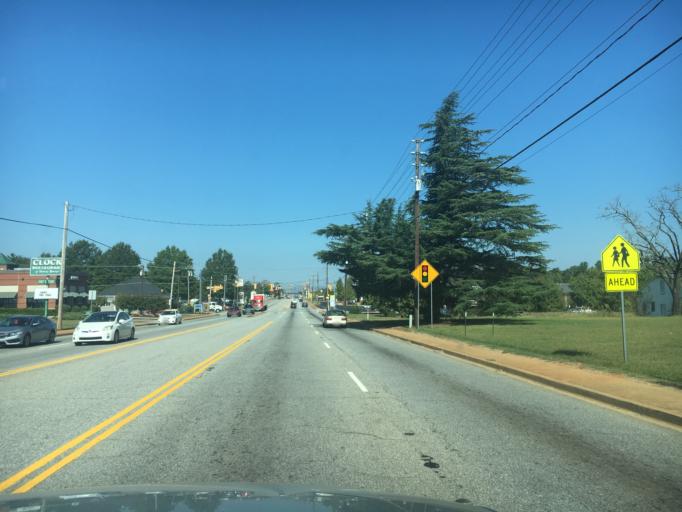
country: US
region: South Carolina
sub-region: Spartanburg County
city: Boiling Springs
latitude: 35.0432
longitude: -81.9787
